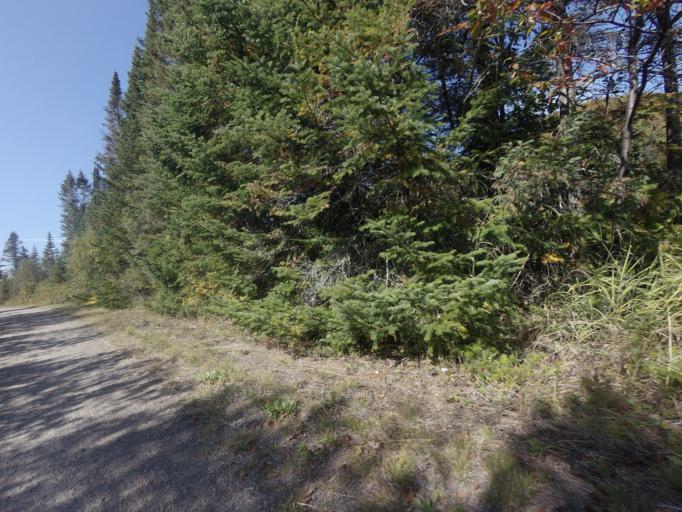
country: CA
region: Quebec
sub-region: Laurentides
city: Sainte-Agathe-des-Monts
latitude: 46.1040
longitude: -74.3659
